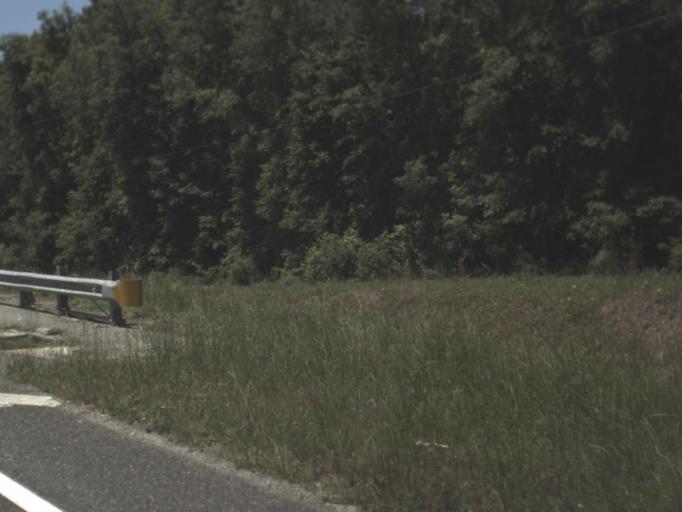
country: US
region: Florida
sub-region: Jefferson County
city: Monticello
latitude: 30.4982
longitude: -83.8800
